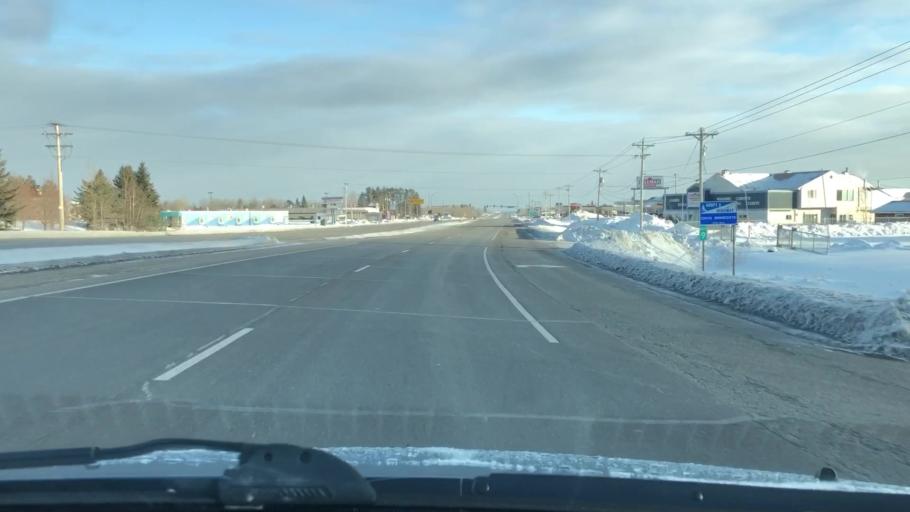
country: US
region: Minnesota
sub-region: Saint Louis County
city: Hermantown
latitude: 46.8359
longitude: -92.2093
